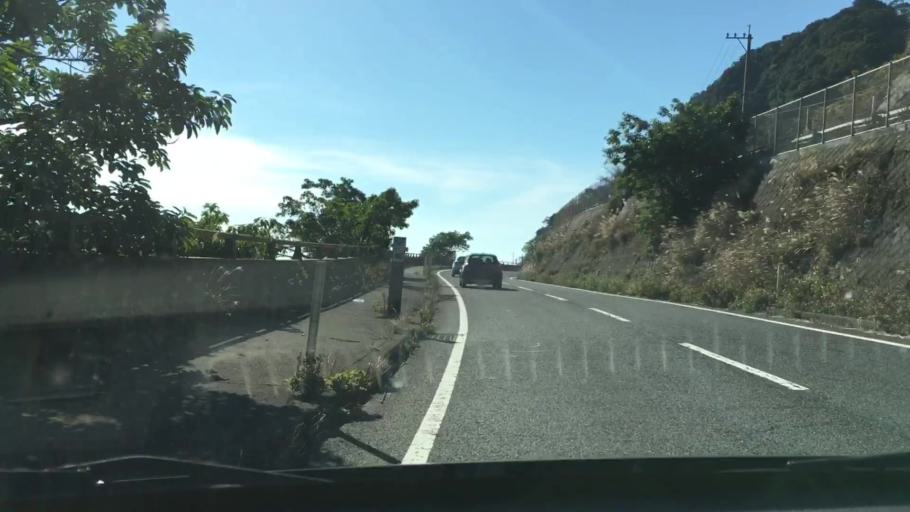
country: JP
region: Kagoshima
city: Kagoshima-shi
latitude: 31.6429
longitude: 130.6029
